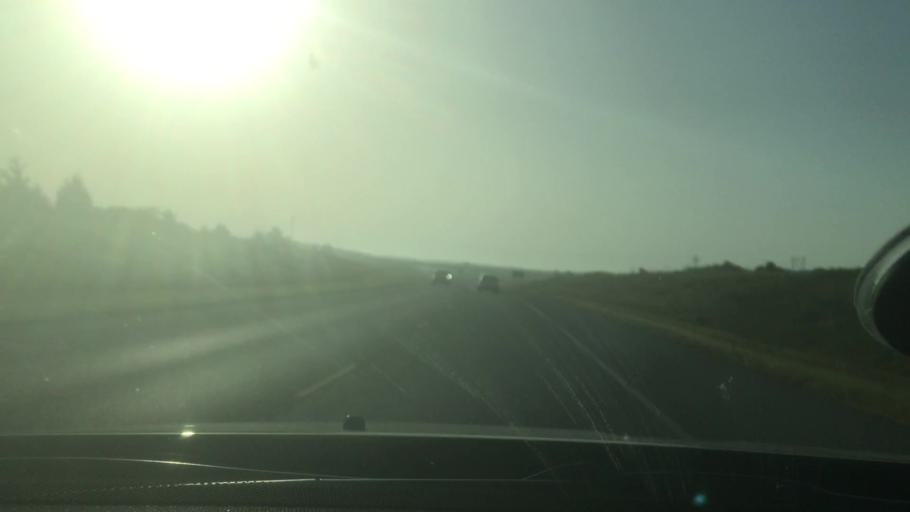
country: US
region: Oklahoma
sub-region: Pontotoc County
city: Ada
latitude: 34.6424
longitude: -96.5389
